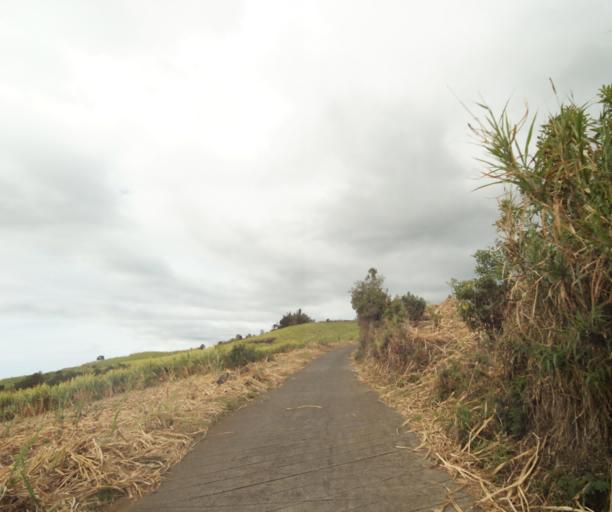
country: RE
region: Reunion
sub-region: Reunion
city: Saint-Paul
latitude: -21.0264
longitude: 55.3200
